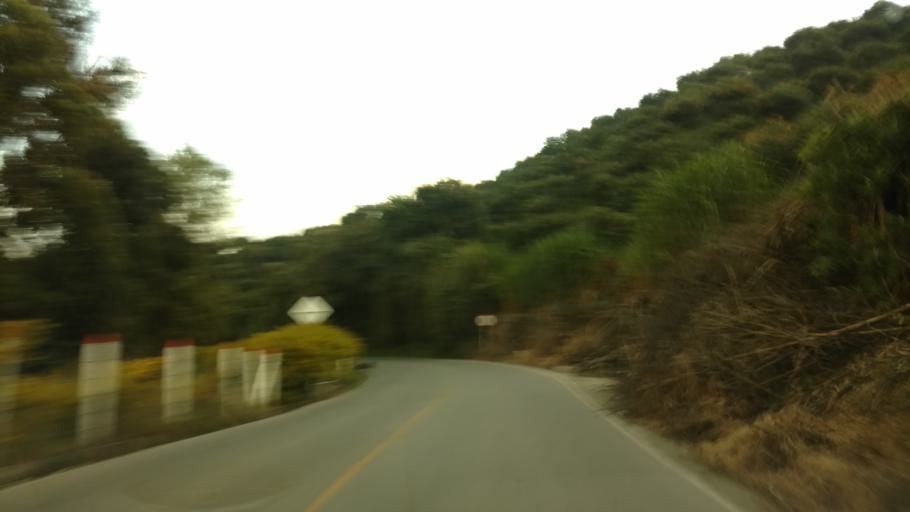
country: CO
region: Caldas
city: Aranzazu
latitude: 5.2859
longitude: -75.4875
